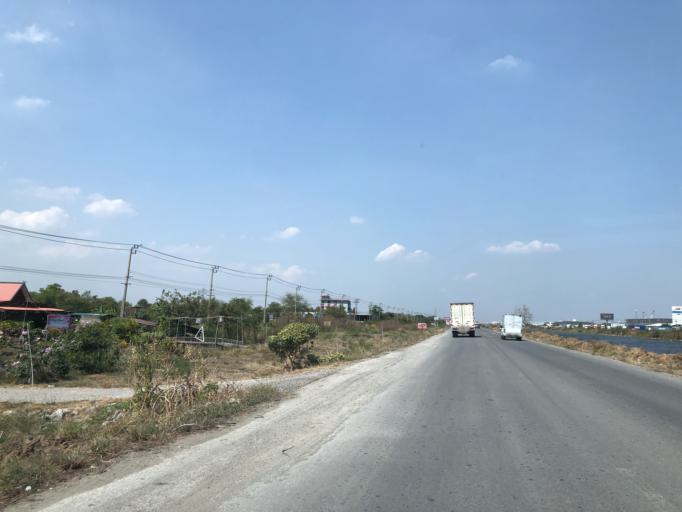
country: TH
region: Samut Prakan
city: Bang Bo District
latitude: 13.5596
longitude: 100.7539
